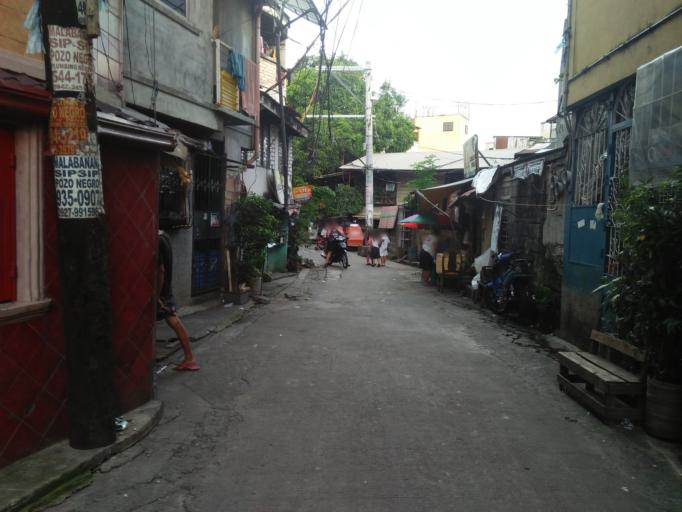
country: PH
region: Metro Manila
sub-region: San Juan
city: San Juan
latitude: 14.6010
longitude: 121.0202
